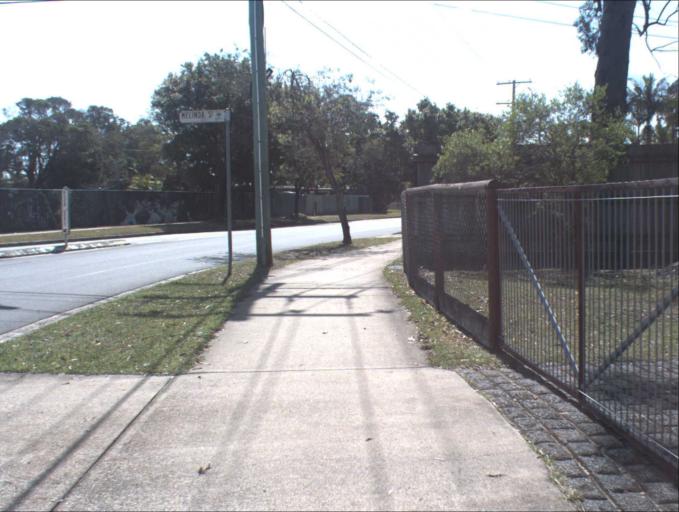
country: AU
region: Queensland
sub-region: Logan
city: Waterford West
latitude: -27.6732
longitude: 153.1108
